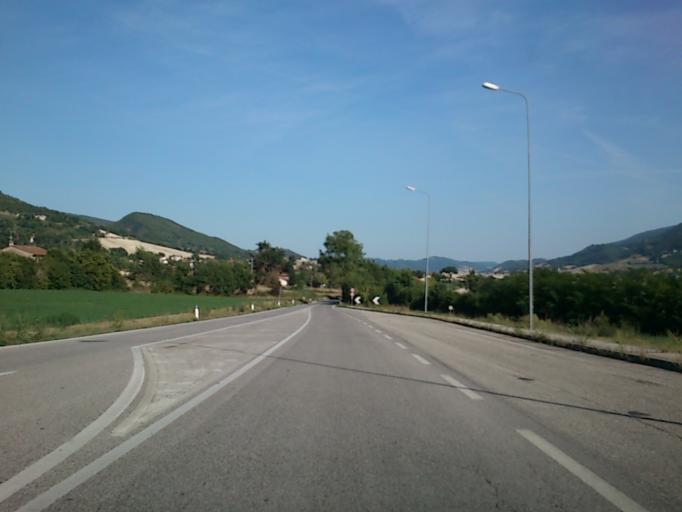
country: IT
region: The Marches
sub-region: Provincia di Pesaro e Urbino
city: Canavaccio
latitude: 43.6985
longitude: 12.6892
